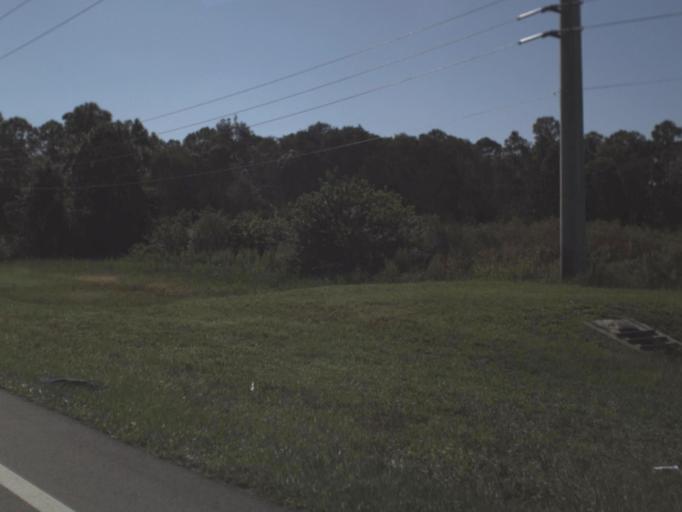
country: US
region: Florida
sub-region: Lee County
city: Gateway
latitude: 26.5867
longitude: -81.7253
